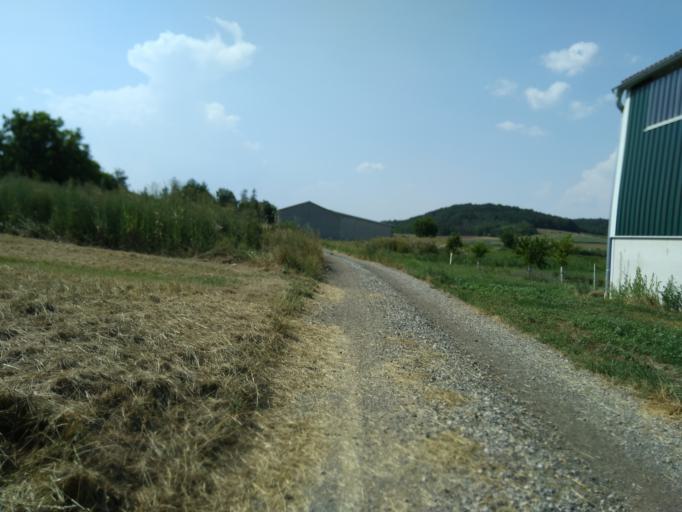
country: AT
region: Lower Austria
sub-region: Politischer Bezirk Ganserndorf
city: Gross-Schweinbarth
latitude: 48.4203
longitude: 16.6330
